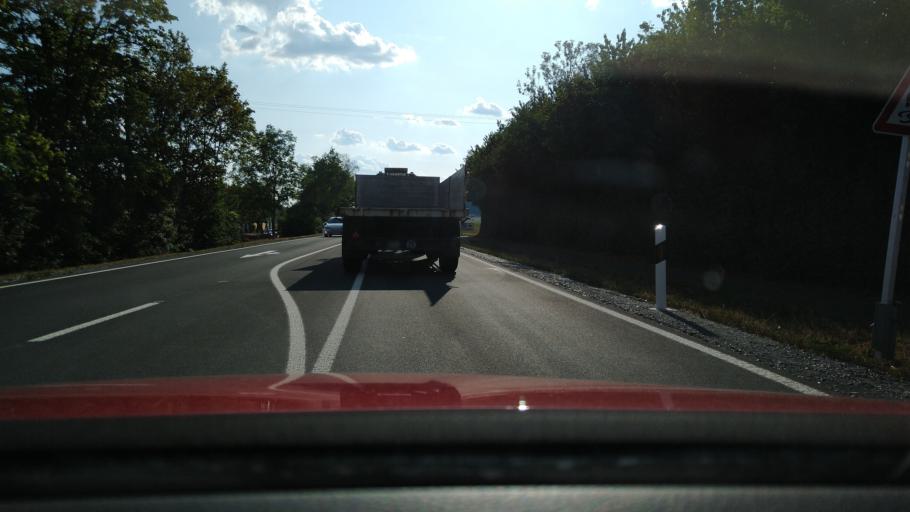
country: DE
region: Bavaria
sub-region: Upper Franconia
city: Mistelgau
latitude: 49.9289
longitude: 11.4618
